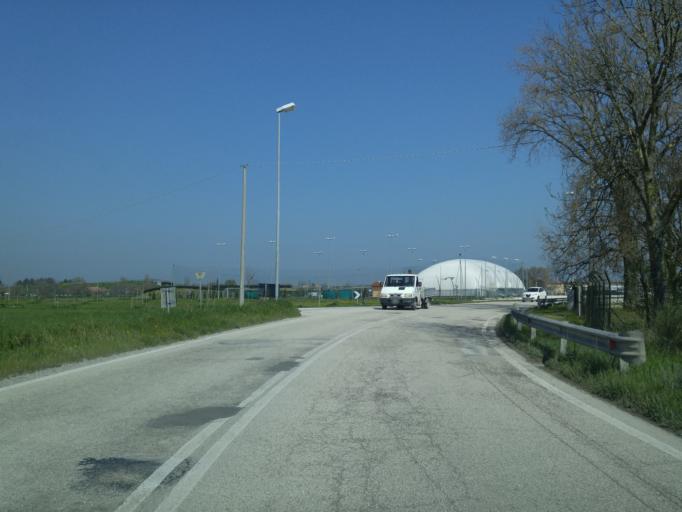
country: IT
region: The Marches
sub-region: Provincia di Pesaro e Urbino
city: Rosciano
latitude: 43.8097
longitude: 13.0143
